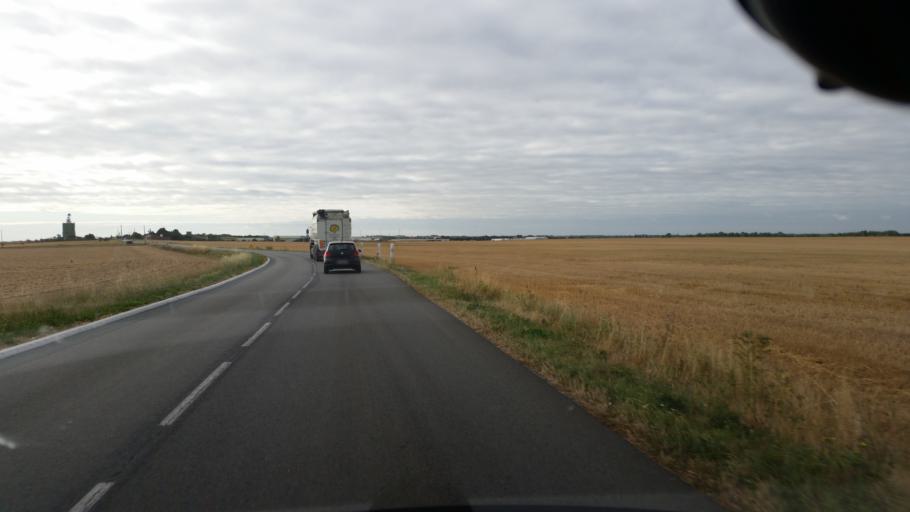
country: FR
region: Poitou-Charentes
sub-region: Departement de la Charente-Maritime
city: Marans
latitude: 46.2939
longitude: -0.9666
